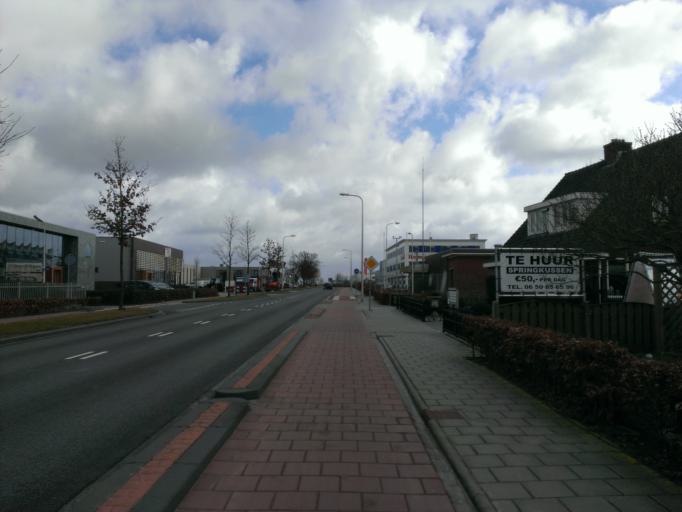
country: NL
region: Drenthe
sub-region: Gemeente Hoogeveen
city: Hoogeveen
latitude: 52.7319
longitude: 6.4830
